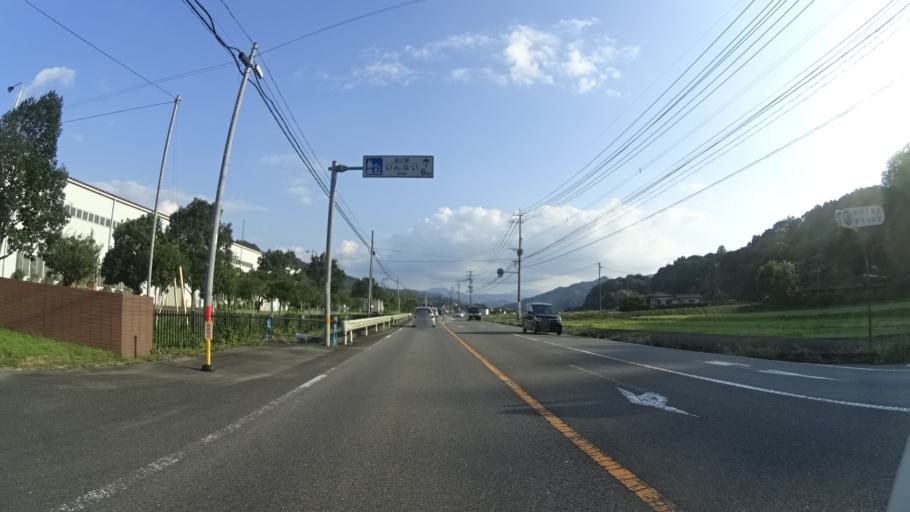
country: JP
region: Oita
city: Bungo-Takada-shi
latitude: 33.4684
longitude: 131.3280
